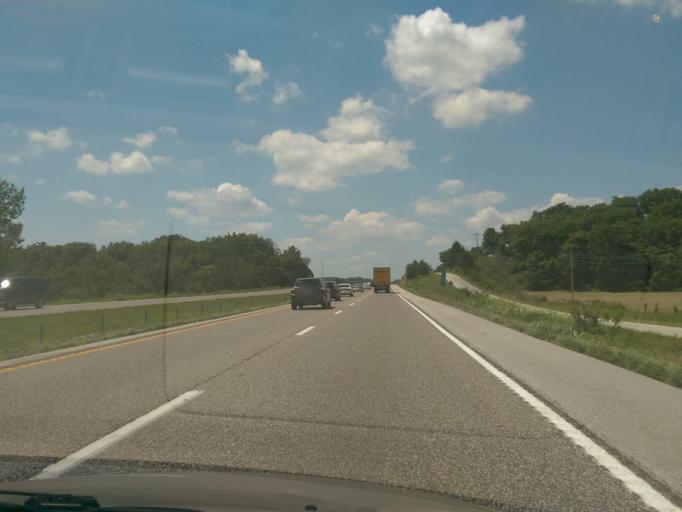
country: US
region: Missouri
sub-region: Boone County
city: Columbia
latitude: 38.9714
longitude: -92.4172
